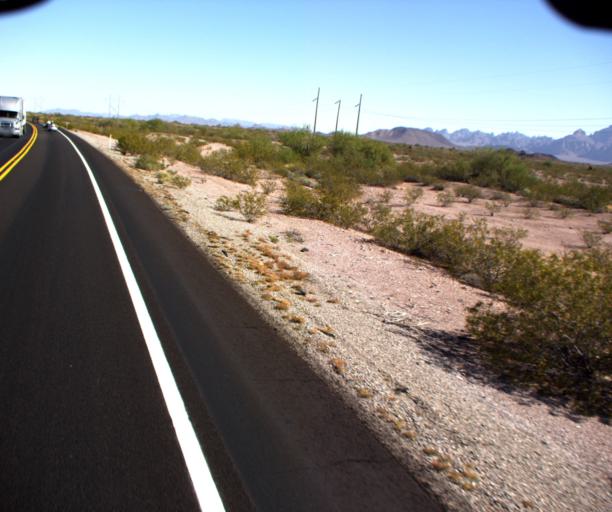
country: US
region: Arizona
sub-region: La Paz County
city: Quartzsite
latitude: 33.3055
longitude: -114.2174
